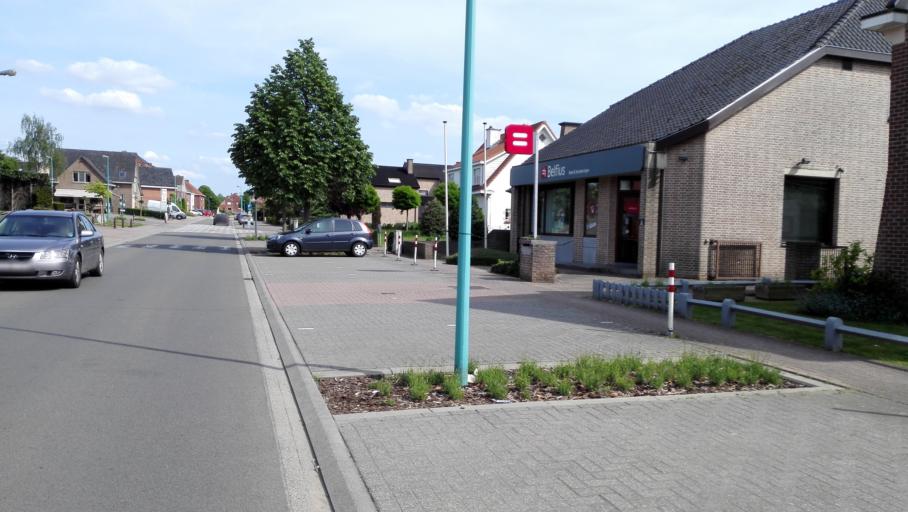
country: BE
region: Flanders
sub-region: Provincie Vlaams-Brabant
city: Holsbeek
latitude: 50.8942
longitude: 4.7712
